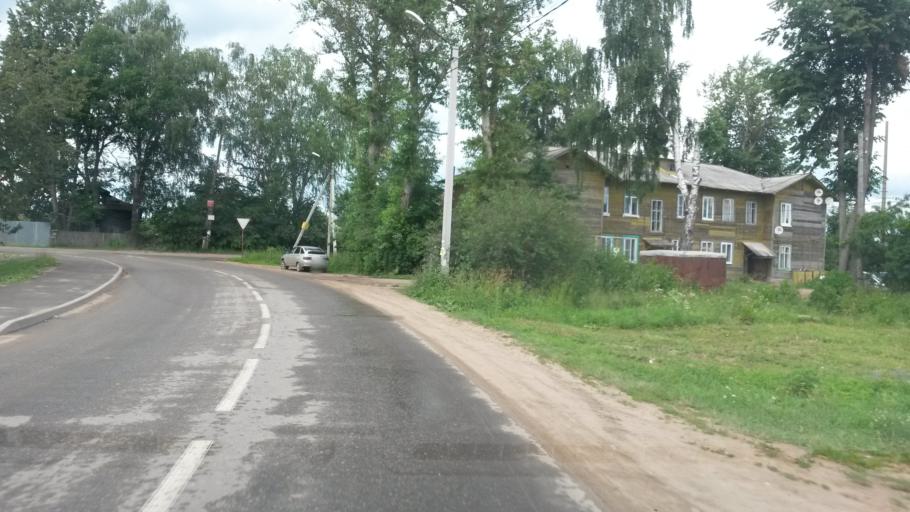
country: RU
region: Jaroslavl
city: Gavrilov-Yam
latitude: 57.3086
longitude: 39.8561
